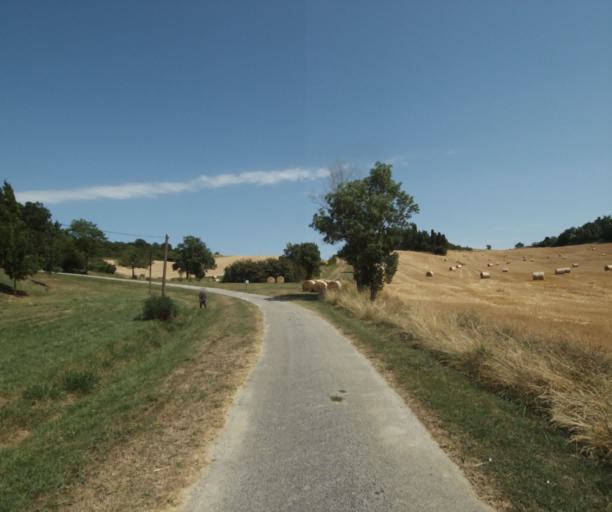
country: FR
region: Midi-Pyrenees
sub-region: Departement de la Haute-Garonne
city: Saint-Felix-Lauragais
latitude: 43.4445
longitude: 1.8715
